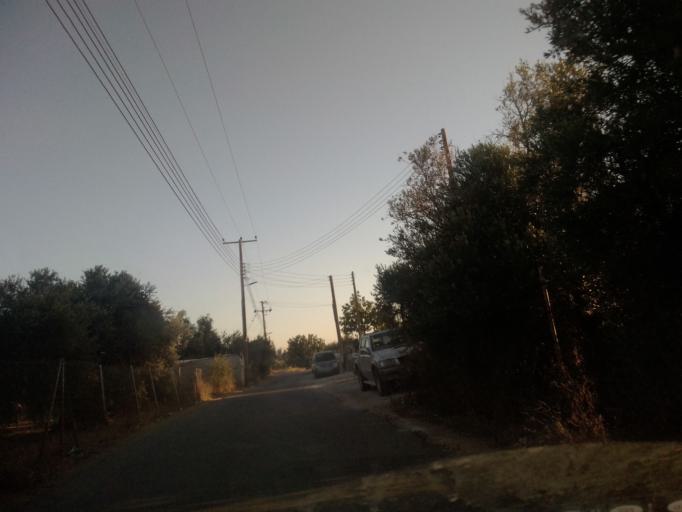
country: CY
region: Limassol
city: Ypsonas
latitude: 34.6769
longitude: 32.9621
